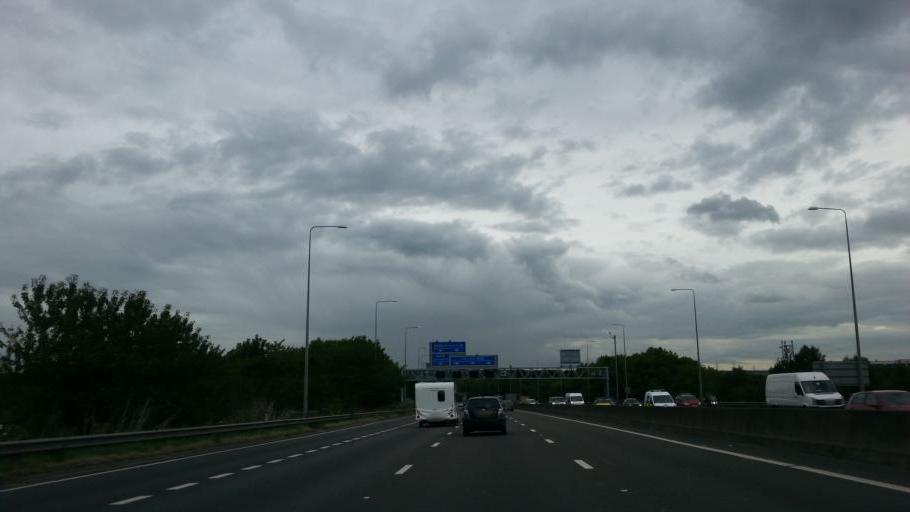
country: GB
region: England
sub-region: Kirklees
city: Cleckheaton
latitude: 53.7243
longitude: -1.7379
